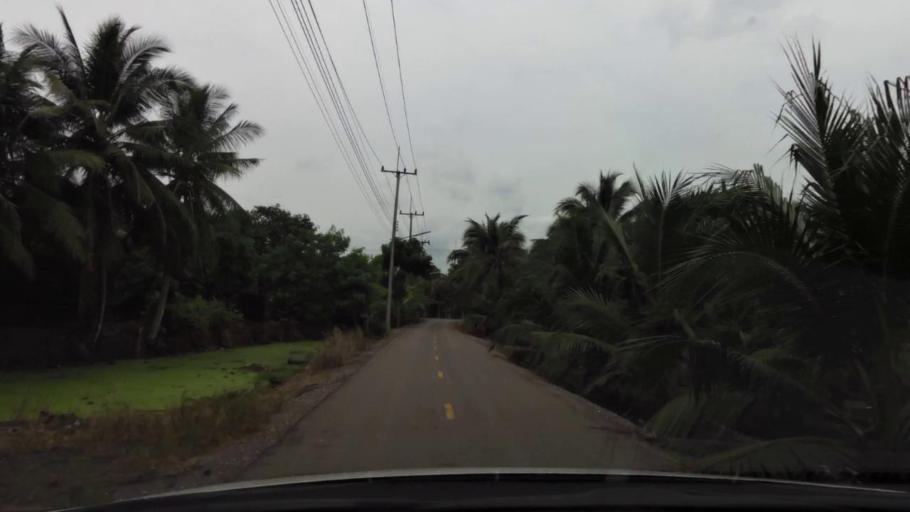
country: TH
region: Samut Sakhon
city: Ban Phaeo
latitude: 13.6125
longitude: 100.0225
